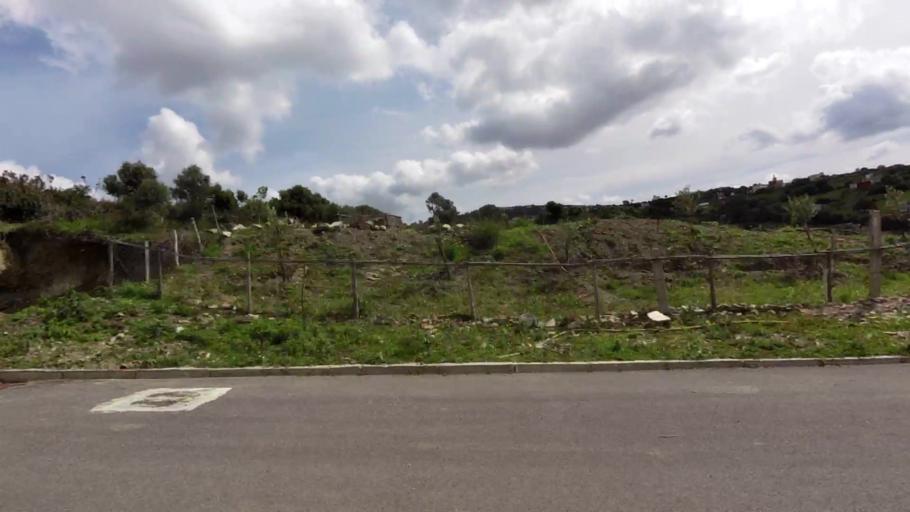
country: MA
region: Tanger-Tetouan
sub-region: Tanger-Assilah
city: Tangier
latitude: 35.7687
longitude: -5.7485
